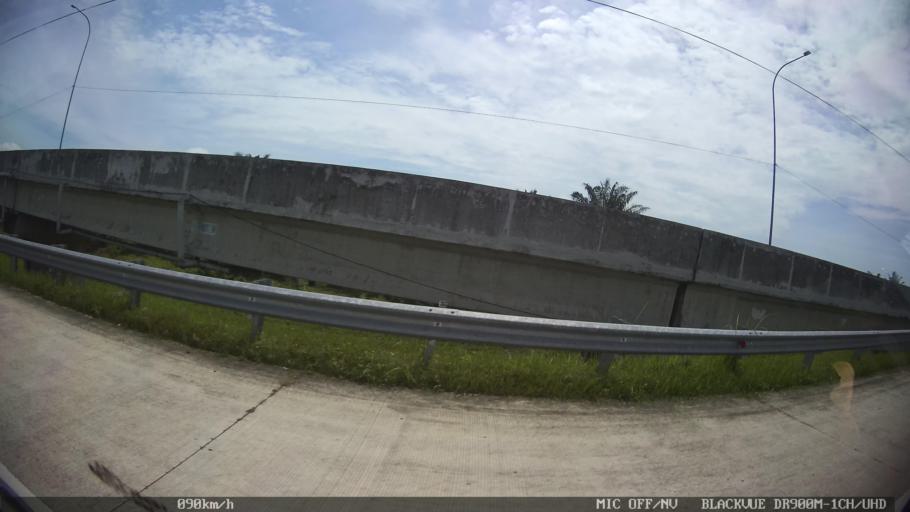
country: ID
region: North Sumatra
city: Percut
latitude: 3.5973
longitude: 98.8434
